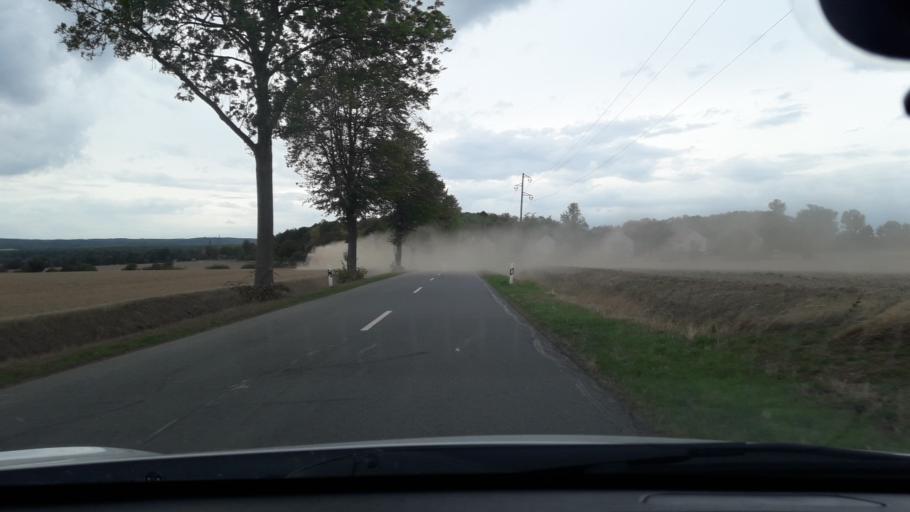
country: DE
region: Lower Saxony
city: Flothe
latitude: 52.0577
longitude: 10.4637
